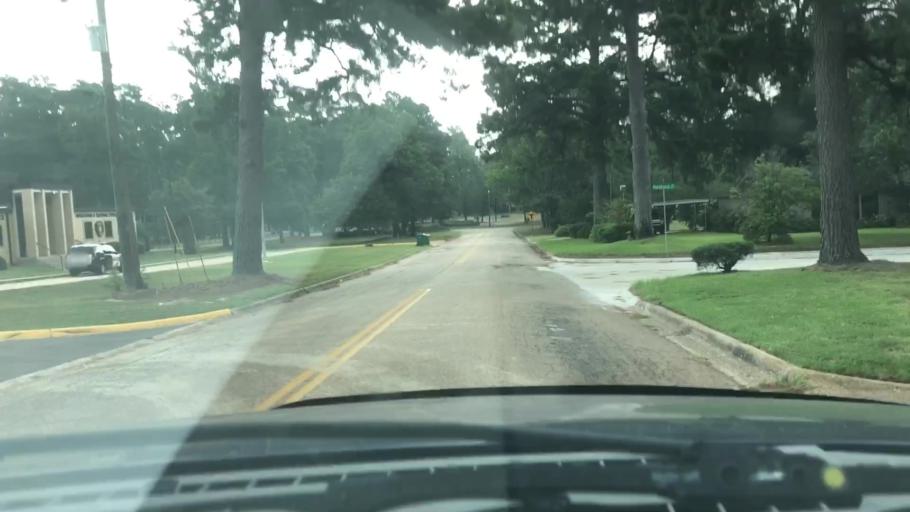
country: US
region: Arkansas
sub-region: Miller County
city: Texarkana
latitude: 33.4608
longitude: -94.0601
